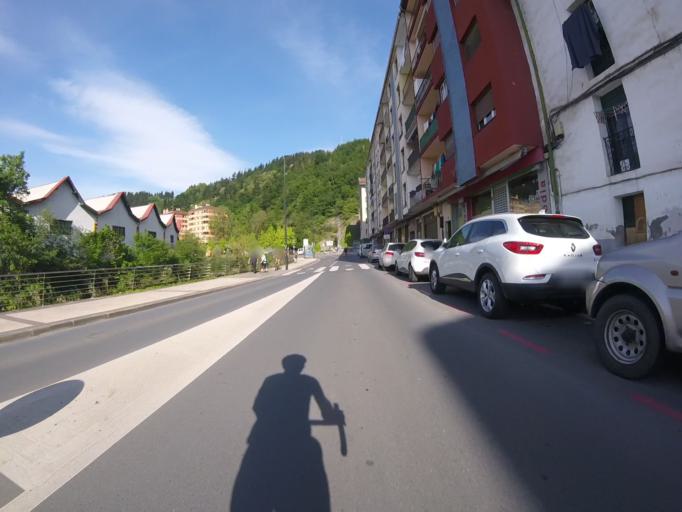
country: ES
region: Basque Country
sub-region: Provincia de Guipuzcoa
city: Villafranca de Ordizia
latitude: 43.0546
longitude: -2.1865
